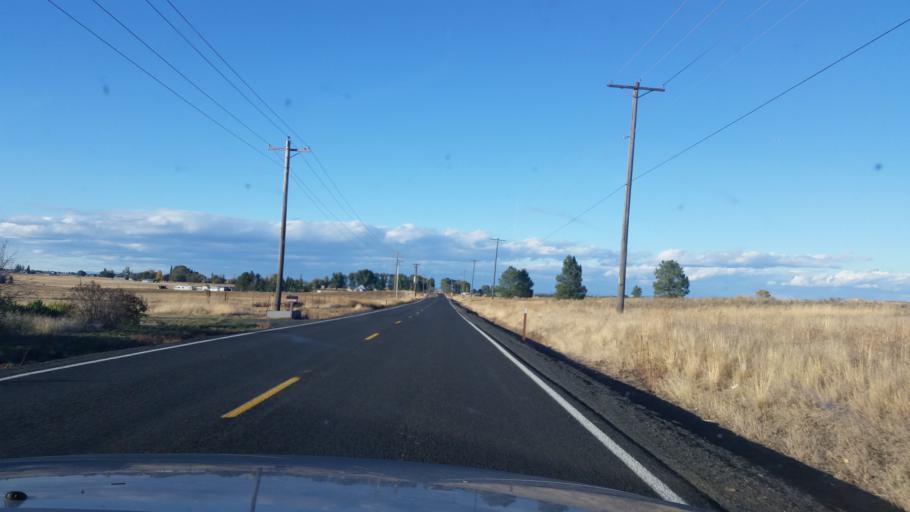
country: US
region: Washington
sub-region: Spokane County
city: Fairchild Air Force Base
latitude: 47.5986
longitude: -117.6075
